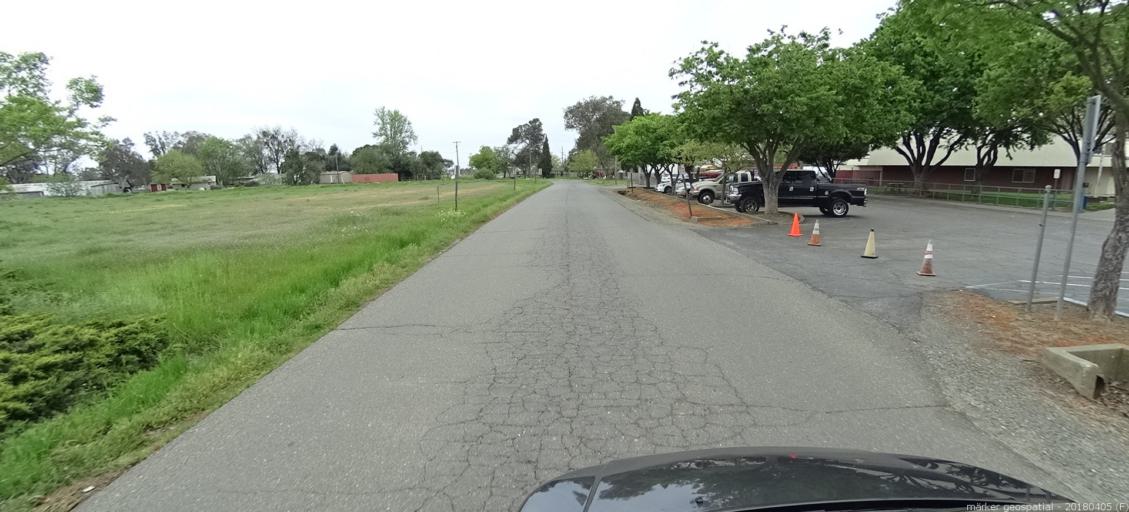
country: US
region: California
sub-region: Sacramento County
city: Herald
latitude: 38.2946
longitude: -121.2419
